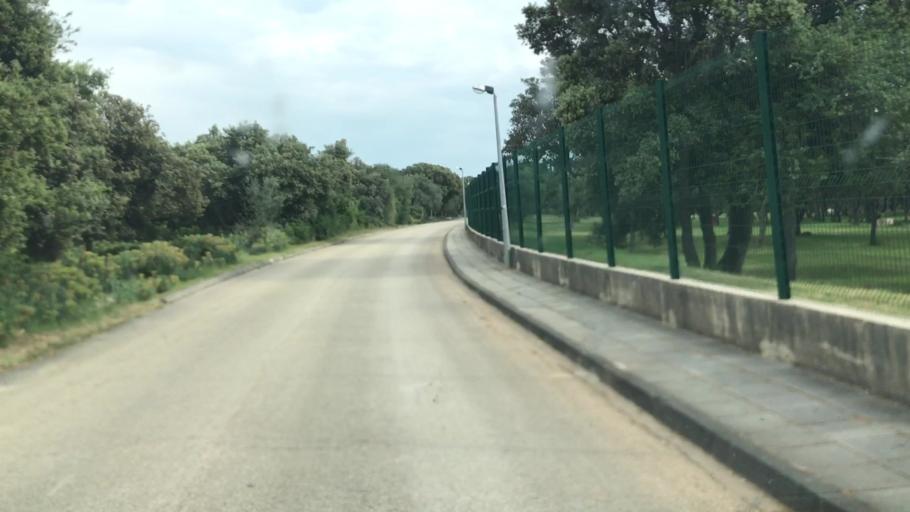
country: HR
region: Licko-Senjska
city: Novalja
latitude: 44.5429
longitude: 14.8839
